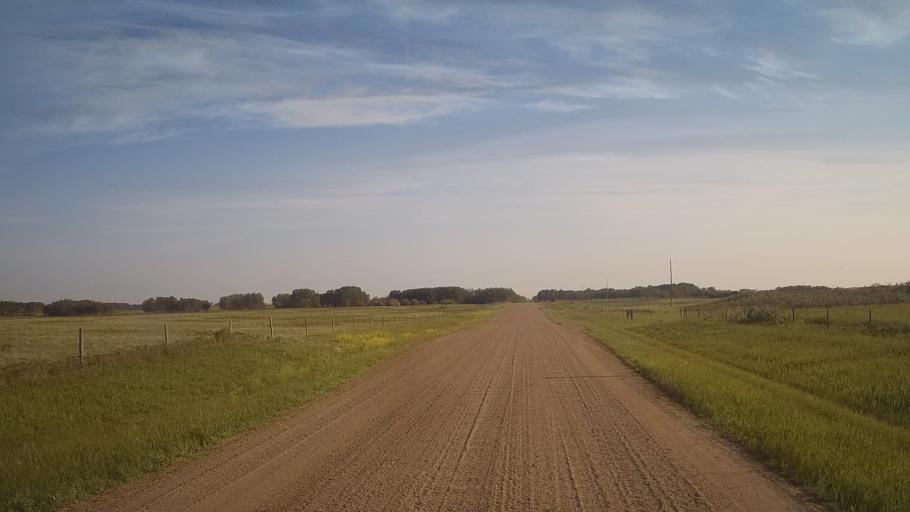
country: CA
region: Saskatchewan
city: Saskatoon
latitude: 51.8249
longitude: -106.5239
